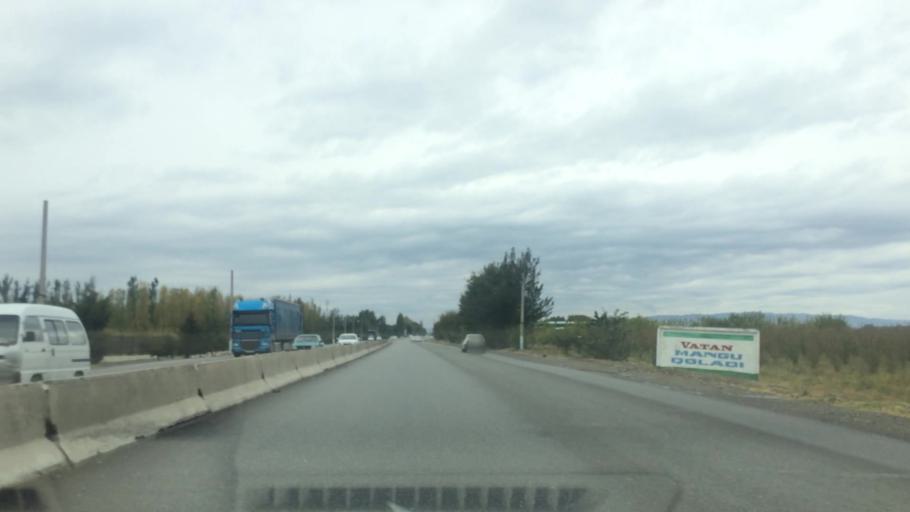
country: UZ
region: Jizzax
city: Jizzax
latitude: 40.0166
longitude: 67.6073
